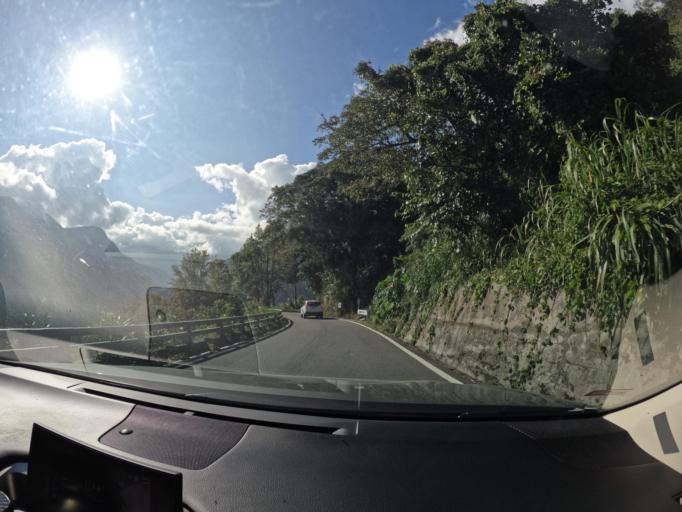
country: TW
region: Taiwan
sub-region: Taitung
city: Taitung
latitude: 23.1936
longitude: 121.0204
